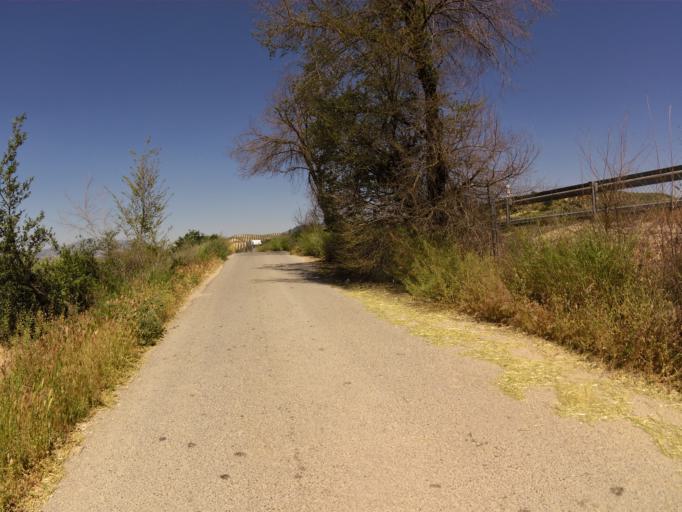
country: ES
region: Andalusia
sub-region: Provincia de Granada
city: Salar
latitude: 37.1630
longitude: -4.1042
